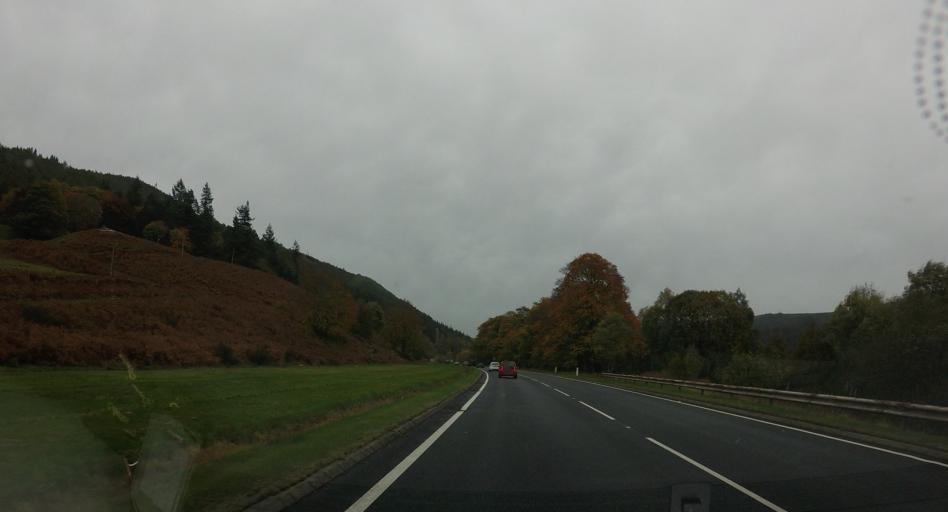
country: GB
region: Scotland
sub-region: Perth and Kinross
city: Bankfoot
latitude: 56.5867
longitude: -3.6229
